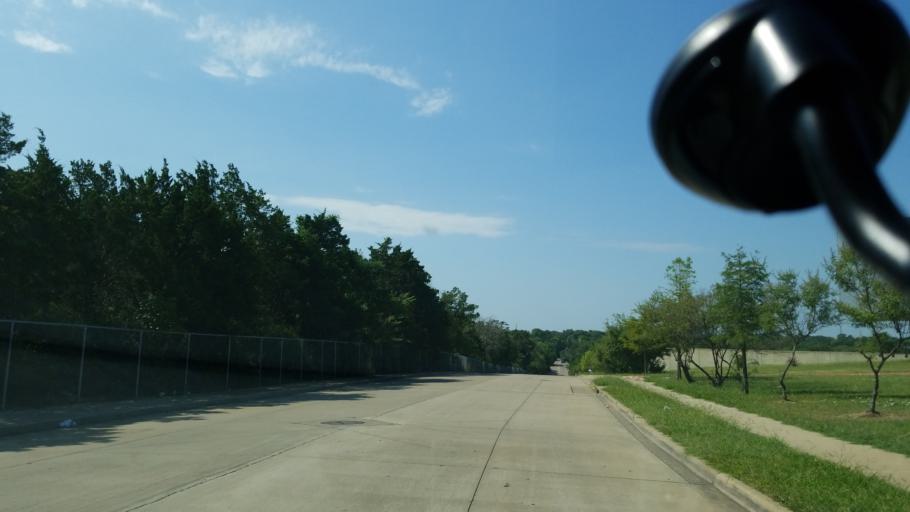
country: US
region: Texas
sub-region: Dallas County
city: Cockrell Hill
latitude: 32.7110
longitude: -96.8659
